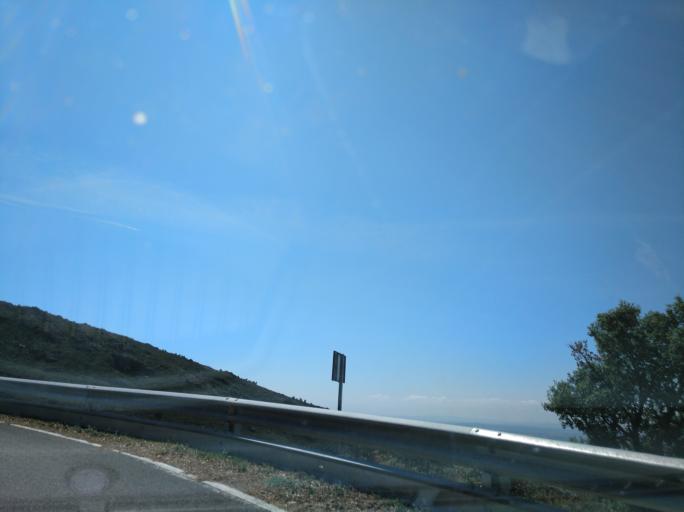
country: ES
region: Catalonia
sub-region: Provincia de Girona
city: Pau
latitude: 42.3296
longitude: 3.1354
